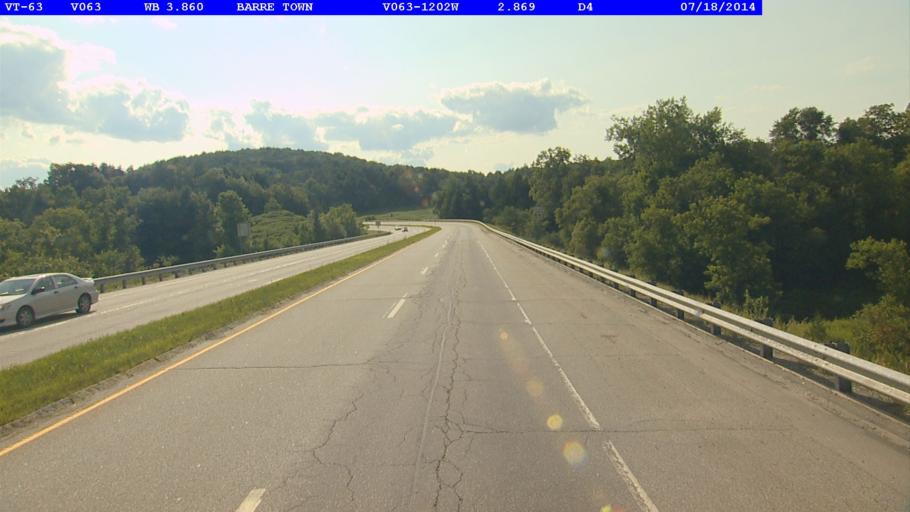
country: US
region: Vermont
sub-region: Washington County
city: South Barre
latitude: 44.1737
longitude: -72.5082
